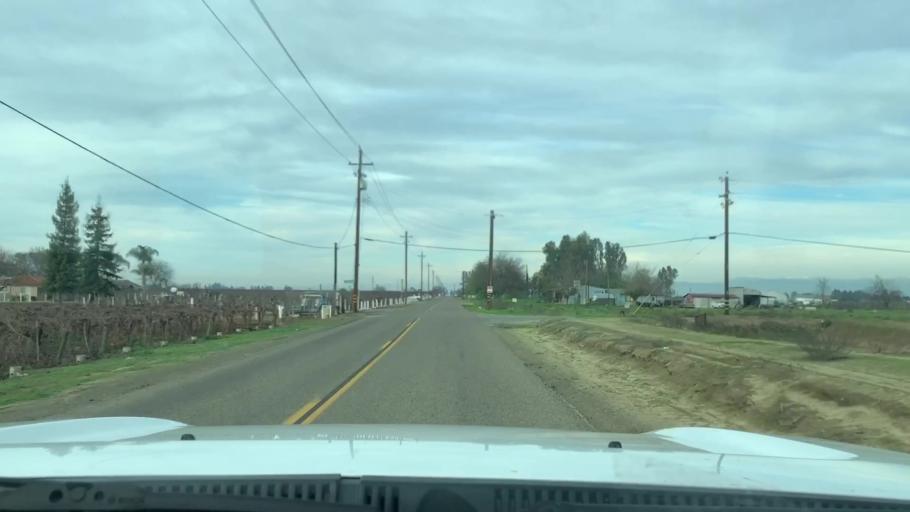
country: US
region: California
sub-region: Fresno County
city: Selma
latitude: 36.5830
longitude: -119.5749
